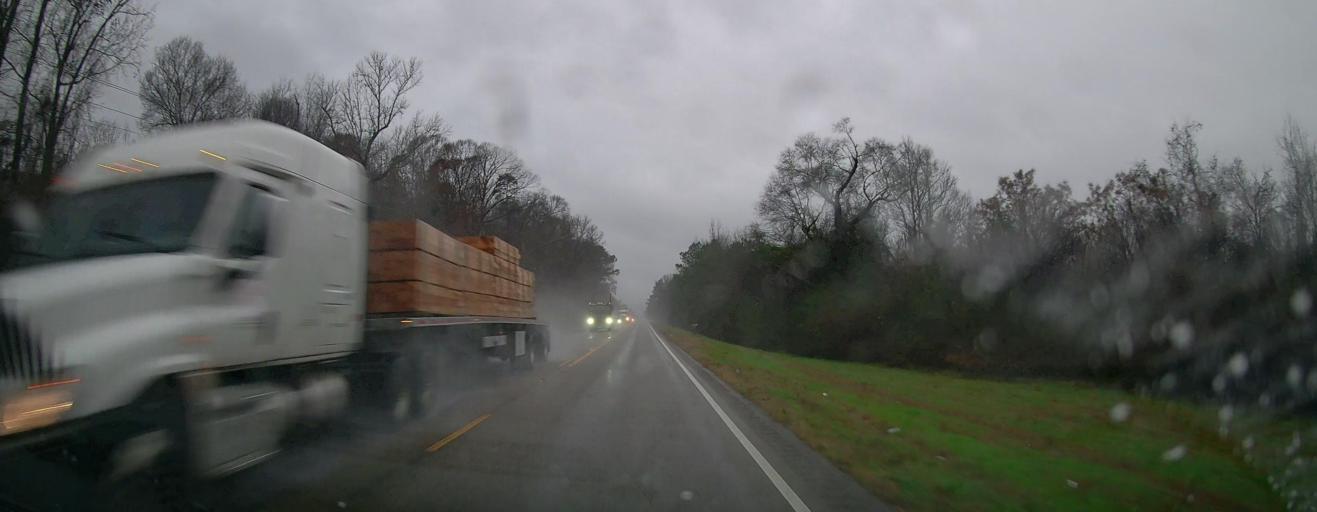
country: US
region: Alabama
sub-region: Autauga County
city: Prattville
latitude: 32.4764
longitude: -86.5246
